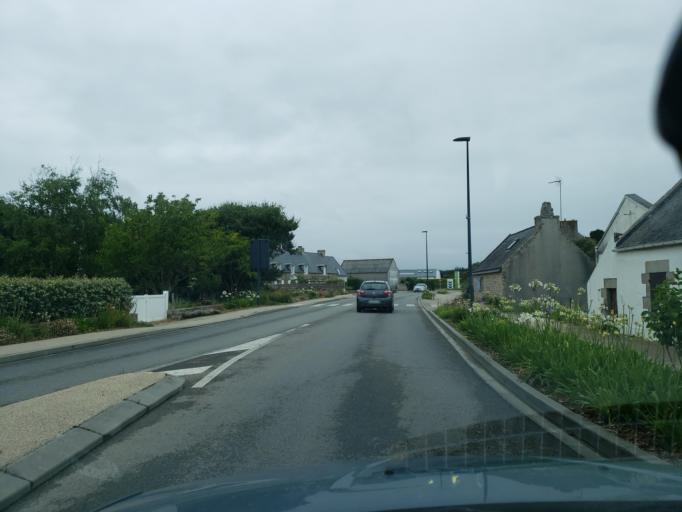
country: FR
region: Brittany
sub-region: Departement du Finistere
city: Plomeur
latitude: 47.8138
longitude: -4.3358
